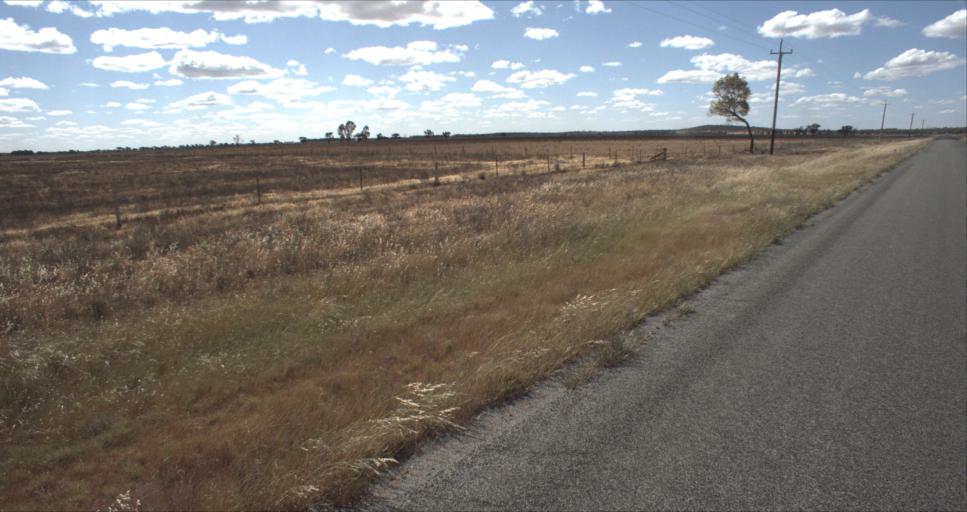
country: AU
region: New South Wales
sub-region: Leeton
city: Leeton
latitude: -34.4556
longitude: 146.2537
